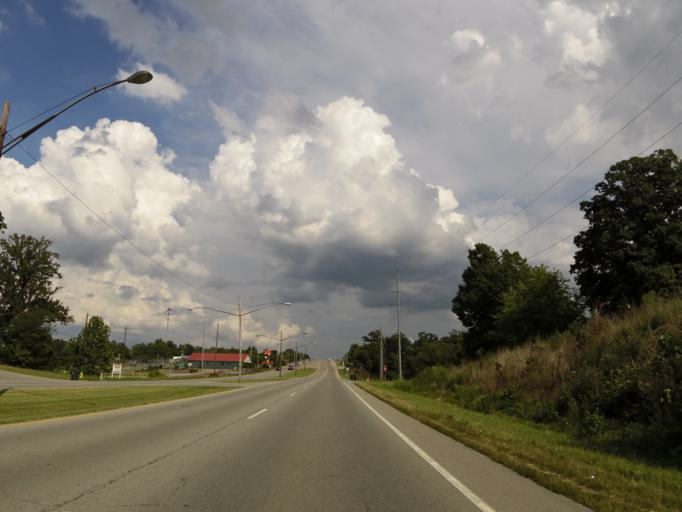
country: US
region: Tennessee
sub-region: Dickson County
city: Dickson
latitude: 36.0861
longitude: -87.4065
